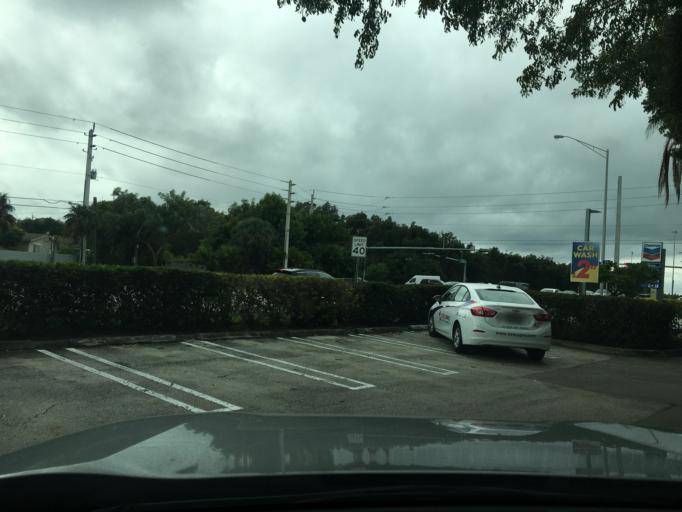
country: US
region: Florida
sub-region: Miami-Dade County
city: Palm Springs North
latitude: 25.9427
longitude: -80.3416
